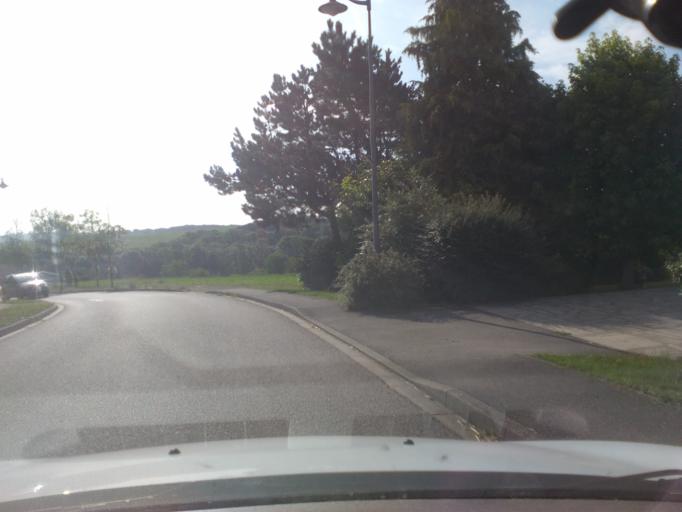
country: FR
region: Lorraine
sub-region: Departement des Vosges
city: Mirecourt
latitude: 48.3080
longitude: 6.0801
